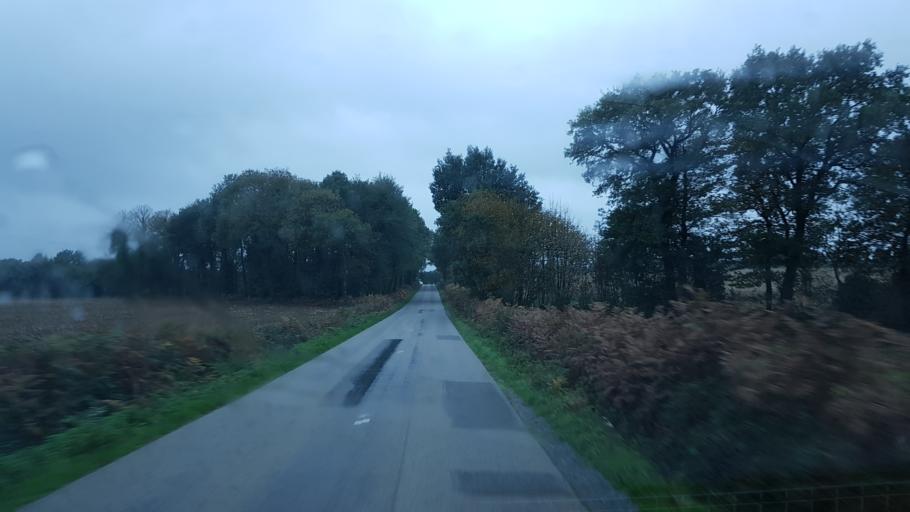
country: FR
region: Brittany
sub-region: Departement du Morbihan
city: Trefflean
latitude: 47.6766
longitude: -2.5924
